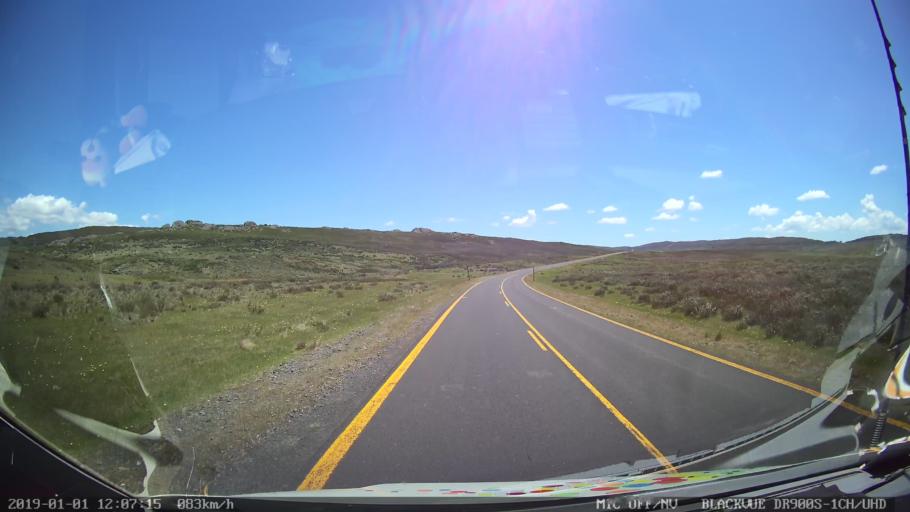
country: AU
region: New South Wales
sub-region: Snowy River
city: Jindabyne
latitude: -35.8354
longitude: 148.4897
